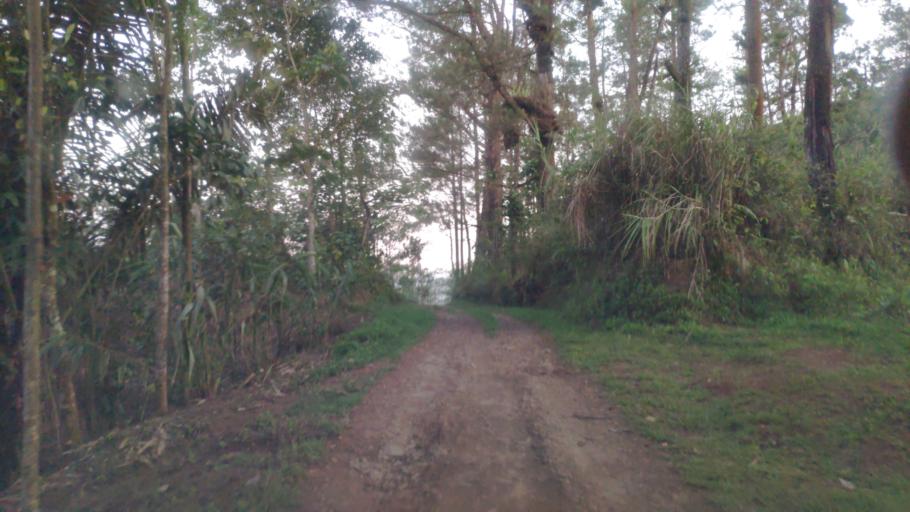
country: ID
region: Central Java
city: Buaran
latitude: -7.2660
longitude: 109.5802
